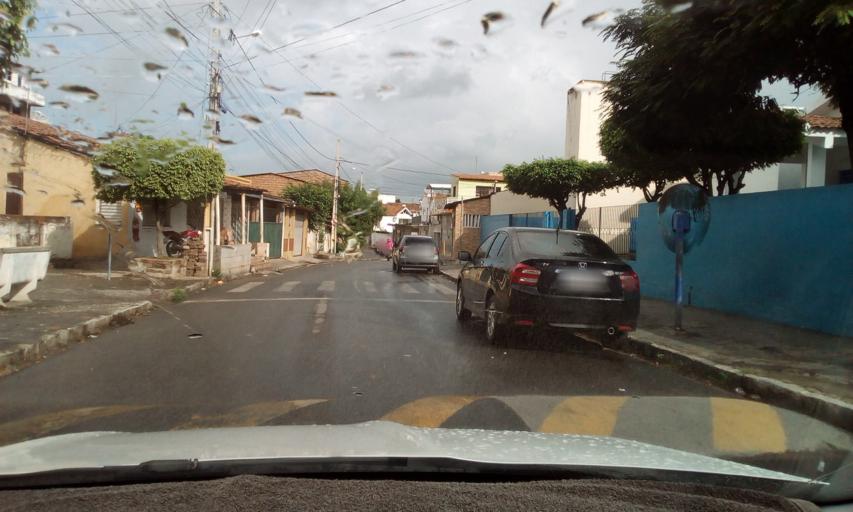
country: BR
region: Paraiba
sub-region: Guarabira
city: Guarabira
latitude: -6.8519
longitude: -35.4992
